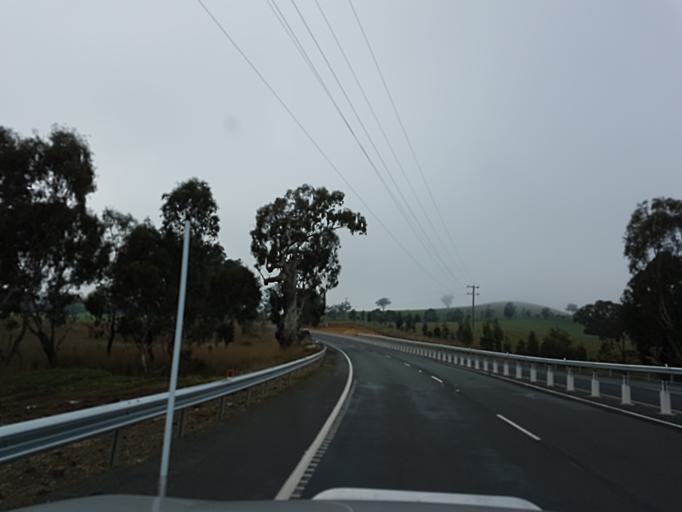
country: AU
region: Victoria
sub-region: Murrindindi
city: Alexandra
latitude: -37.2002
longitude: 145.4704
